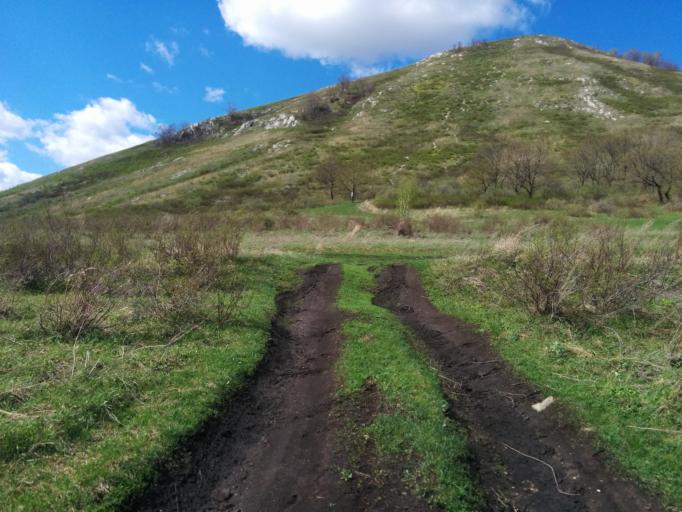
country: RU
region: Bashkortostan
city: Sterlitamak
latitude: 53.7420
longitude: 56.1046
